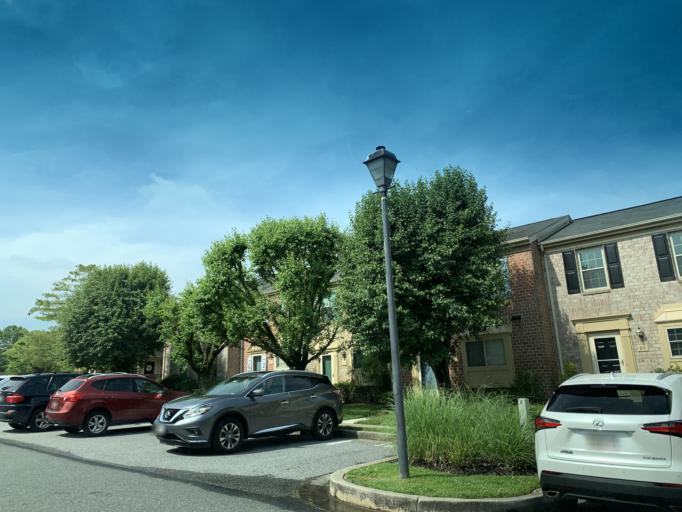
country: US
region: Maryland
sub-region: Baltimore County
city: Perry Hall
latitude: 39.3917
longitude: -76.4724
